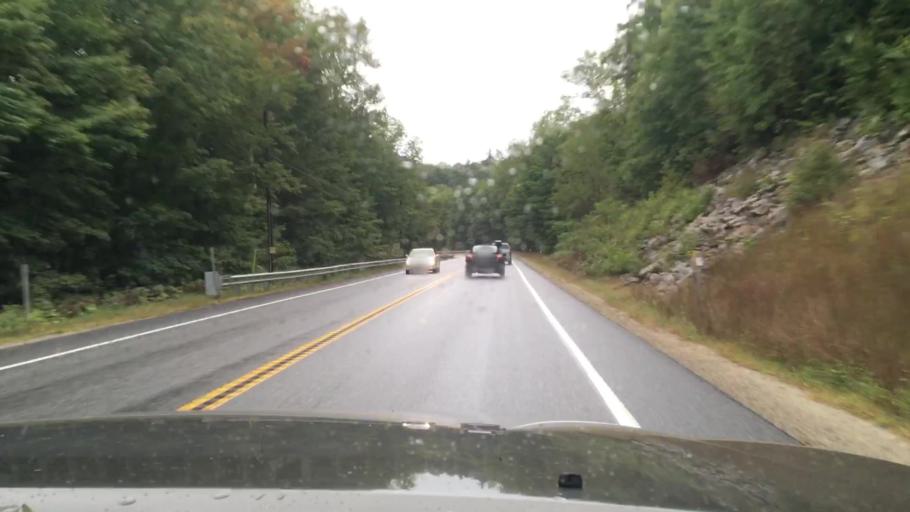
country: US
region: New Hampshire
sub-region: Cheshire County
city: Harrisville
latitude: 43.0671
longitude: -72.0615
